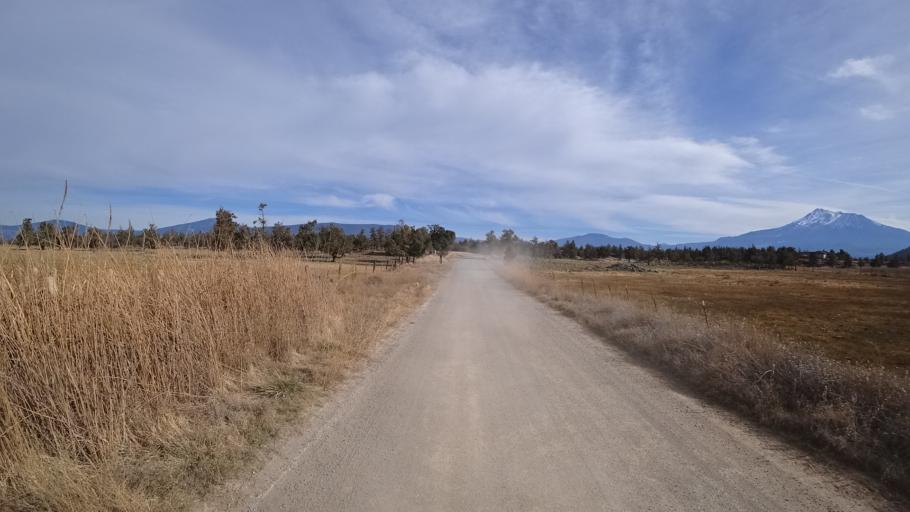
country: US
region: California
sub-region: Siskiyou County
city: Montague
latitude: 41.5954
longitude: -122.4209
